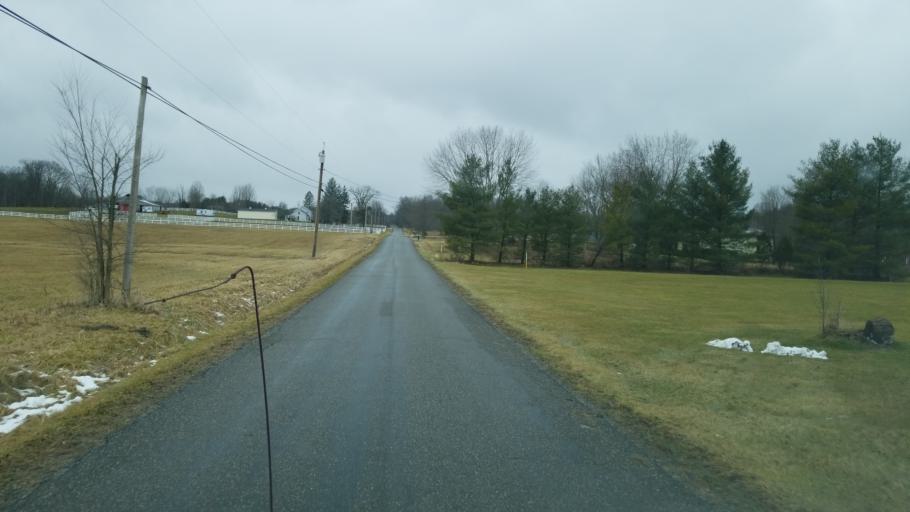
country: US
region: Ohio
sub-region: Portage County
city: Windham
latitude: 41.3394
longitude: -80.9710
